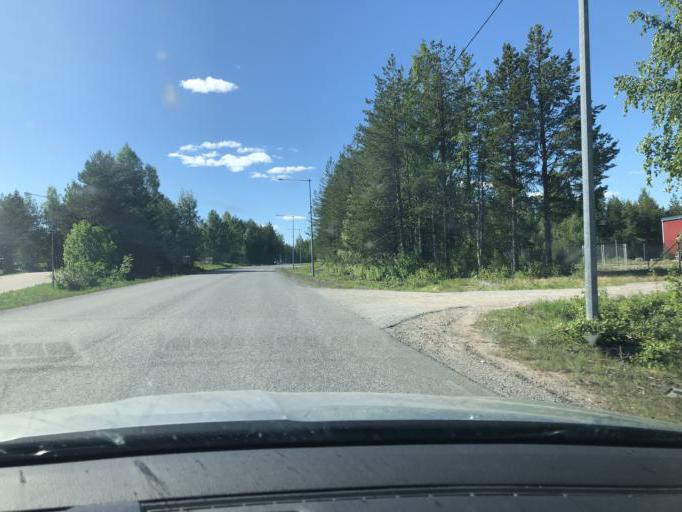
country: SE
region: Norrbotten
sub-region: Kalix Kommun
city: Kalix
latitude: 65.8592
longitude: 23.1631
